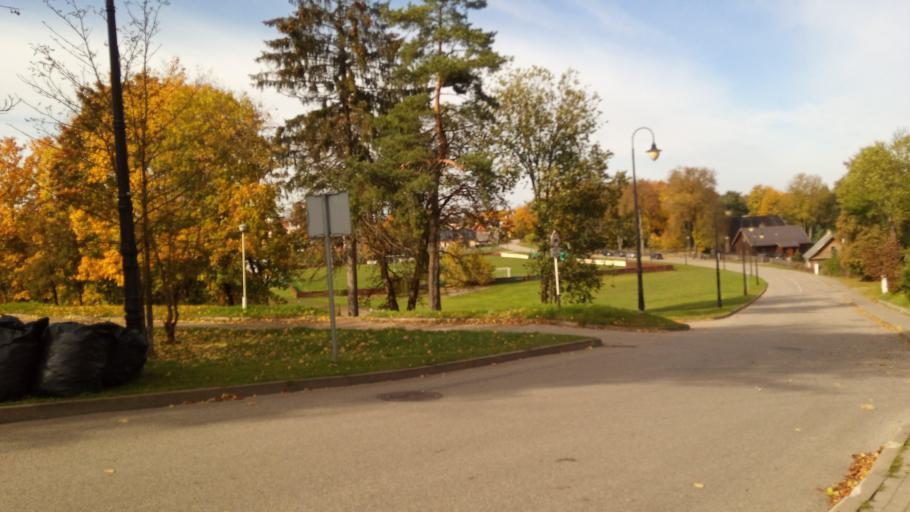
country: LT
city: Trakai
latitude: 54.6389
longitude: 24.9393
